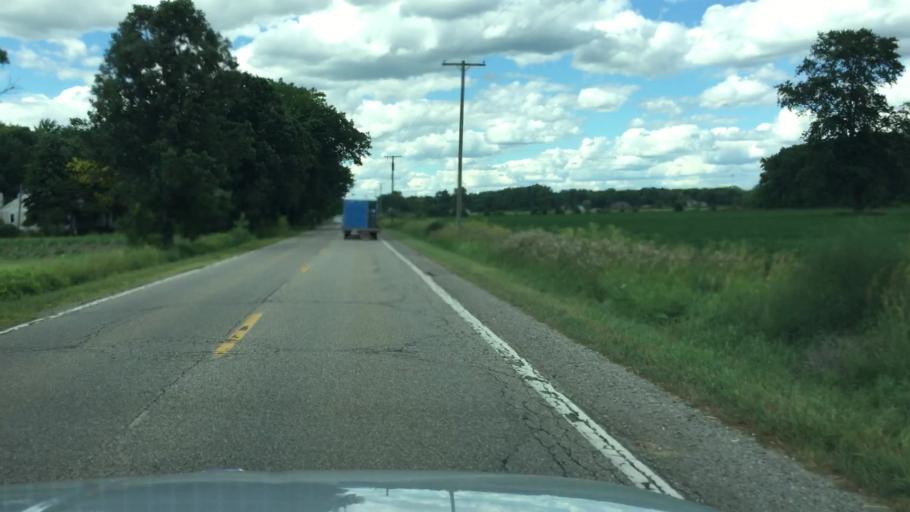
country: US
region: Michigan
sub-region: Macomb County
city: Armada
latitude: 42.8557
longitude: -82.9445
